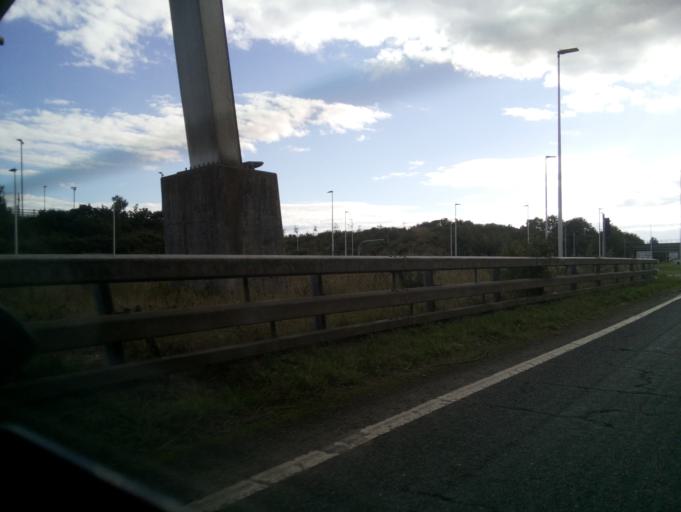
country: GB
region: England
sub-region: Devon
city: Topsham
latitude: 50.7110
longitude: -3.4706
